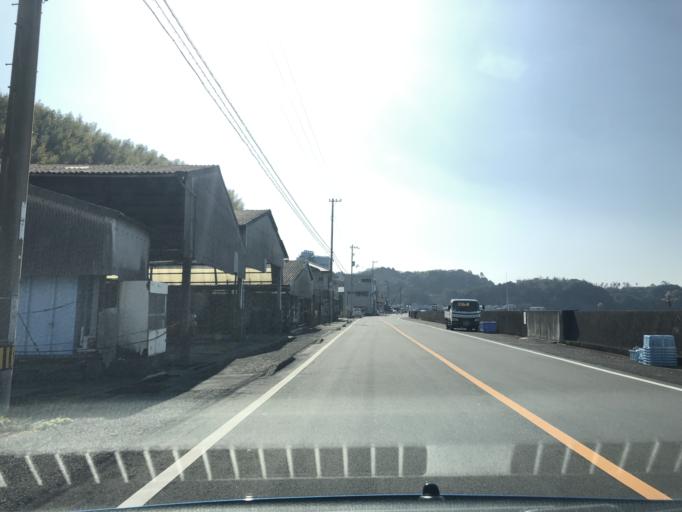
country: JP
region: Kochi
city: Sukumo
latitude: 32.9239
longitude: 132.6955
